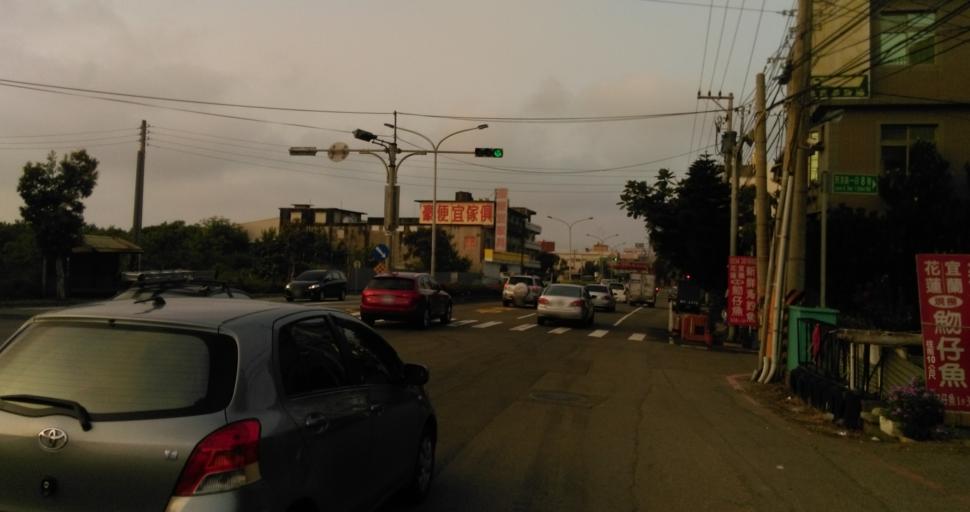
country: TW
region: Taiwan
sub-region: Hsinchu
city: Hsinchu
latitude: 24.8254
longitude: 120.9274
